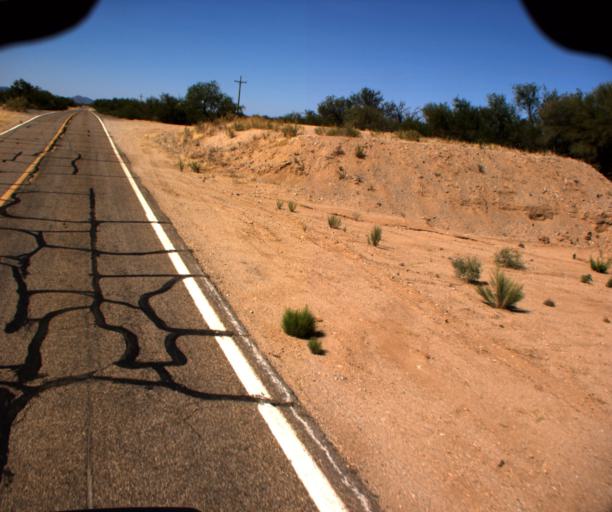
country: US
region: Arizona
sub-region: Pima County
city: Three Points
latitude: 31.9475
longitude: -111.3899
